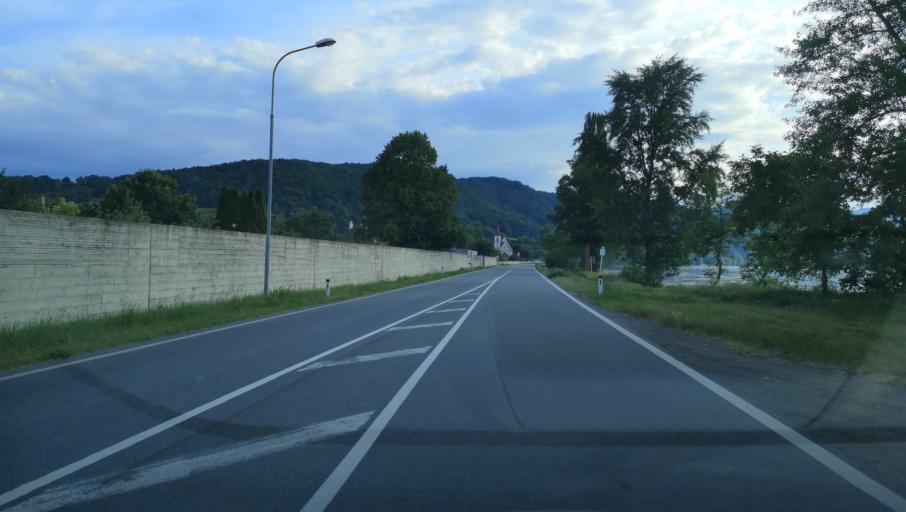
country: AT
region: Lower Austria
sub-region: Politischer Bezirk Krems
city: Weinzierl bei Krems
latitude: 48.3894
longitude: 15.5604
